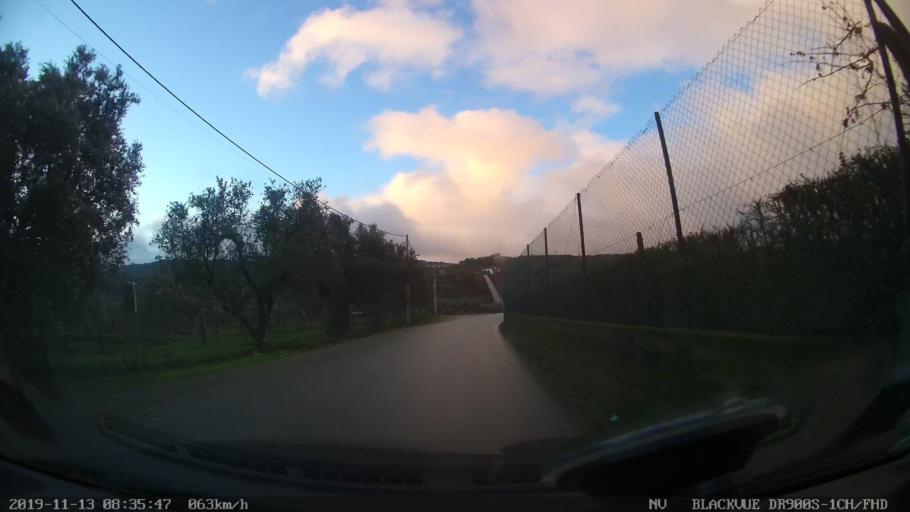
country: PT
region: Vila Real
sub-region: Sabrosa
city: Sabrosa
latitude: 41.2595
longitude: -7.5954
